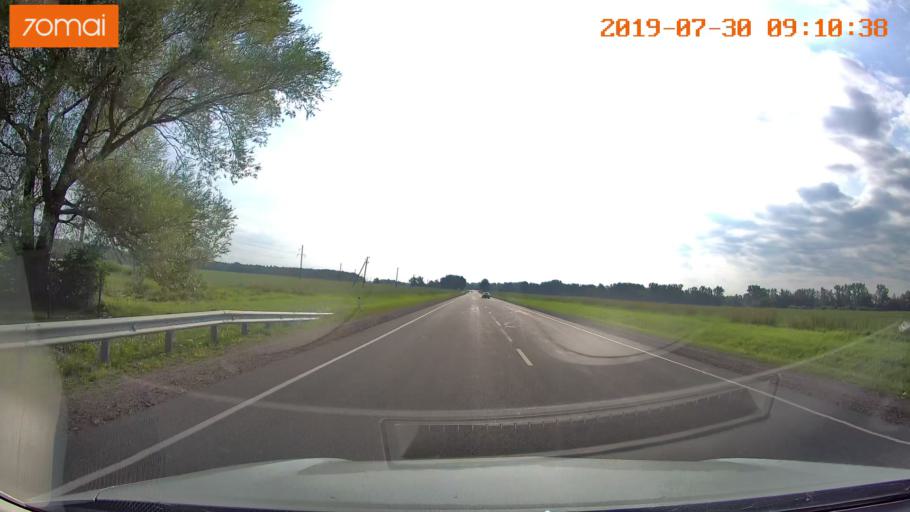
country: RU
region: Kaliningrad
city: Nesterov
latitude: 54.6121
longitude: 22.4307
